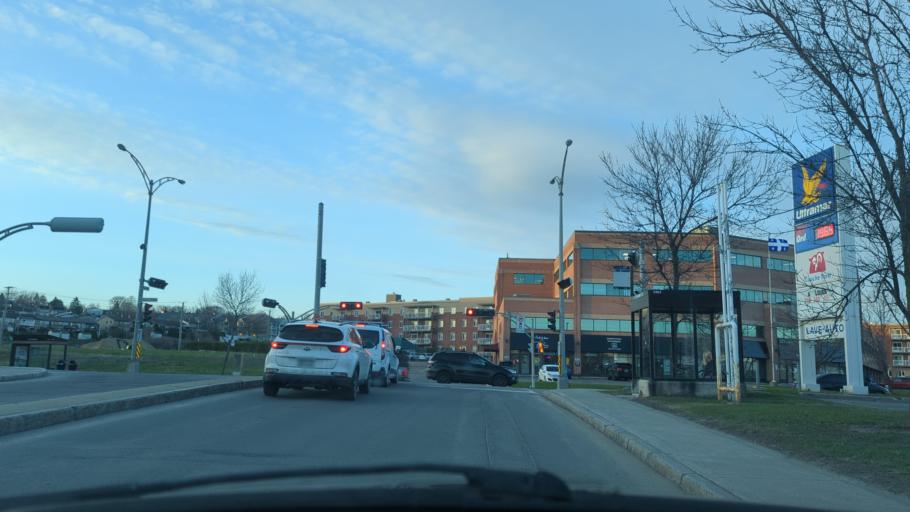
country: CA
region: Quebec
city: Quebec
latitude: 46.8450
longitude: -71.2665
